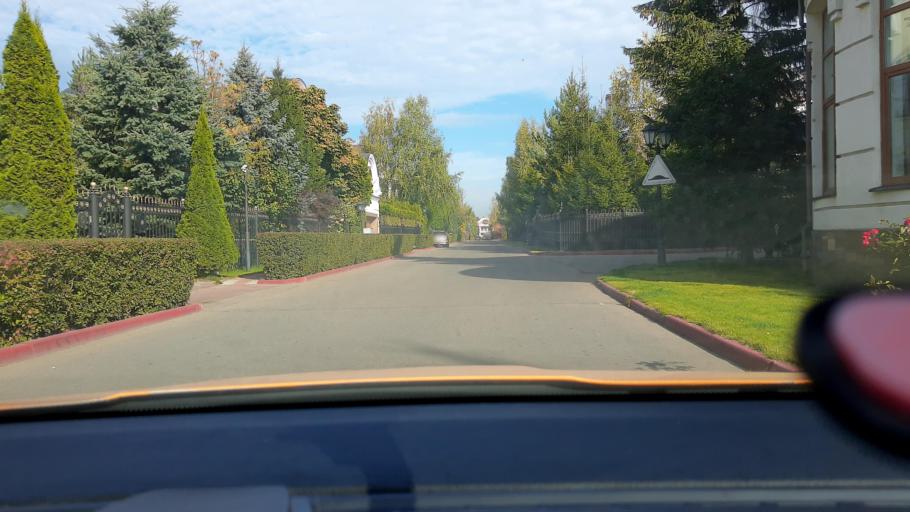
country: RU
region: Moskovskaya
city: Opalikha
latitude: 55.8009
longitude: 37.2067
